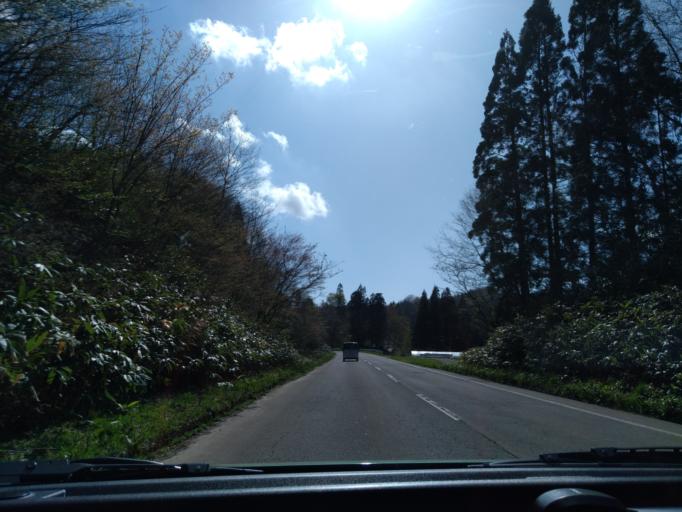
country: JP
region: Akita
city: Akita
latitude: 39.6944
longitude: 140.2308
